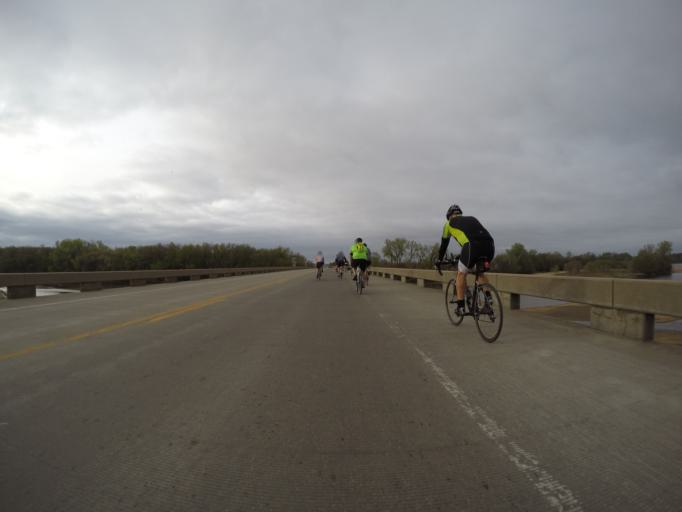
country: US
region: Kansas
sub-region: Pottawatomie County
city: Wamego
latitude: 39.1977
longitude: -96.3052
